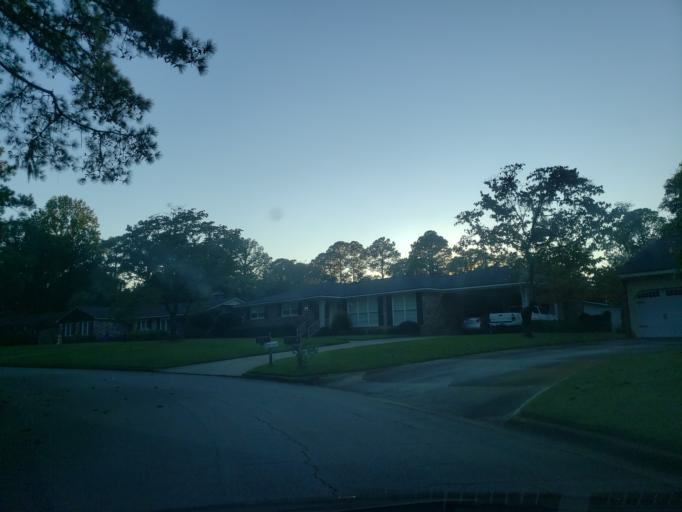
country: US
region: Georgia
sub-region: Chatham County
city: Isle of Hope
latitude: 31.9938
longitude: -81.0933
